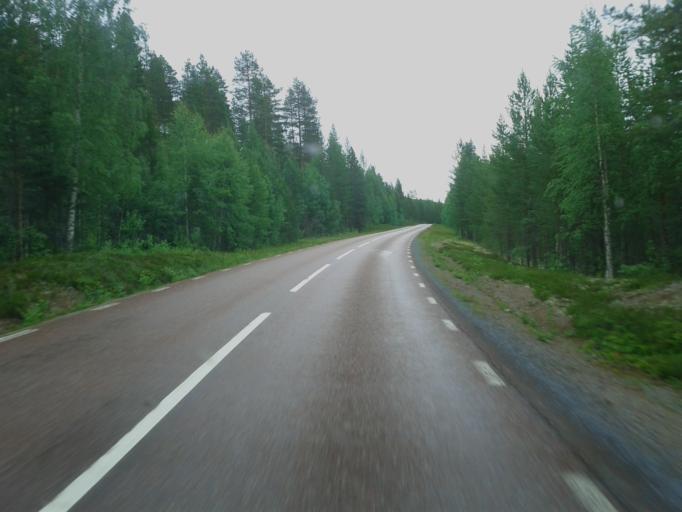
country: NO
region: Hedmark
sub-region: Trysil
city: Innbygda
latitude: 61.7852
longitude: 12.9338
